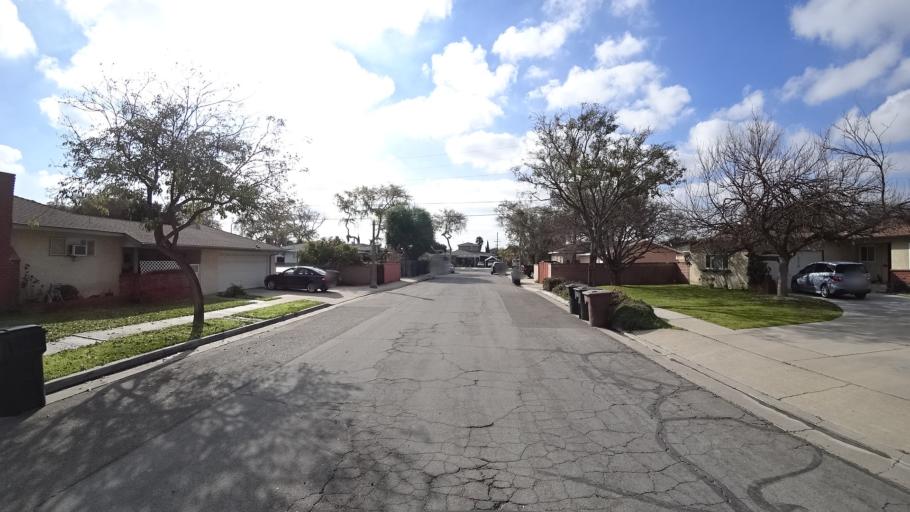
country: US
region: California
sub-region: Orange County
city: Anaheim
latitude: 33.8237
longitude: -117.9143
